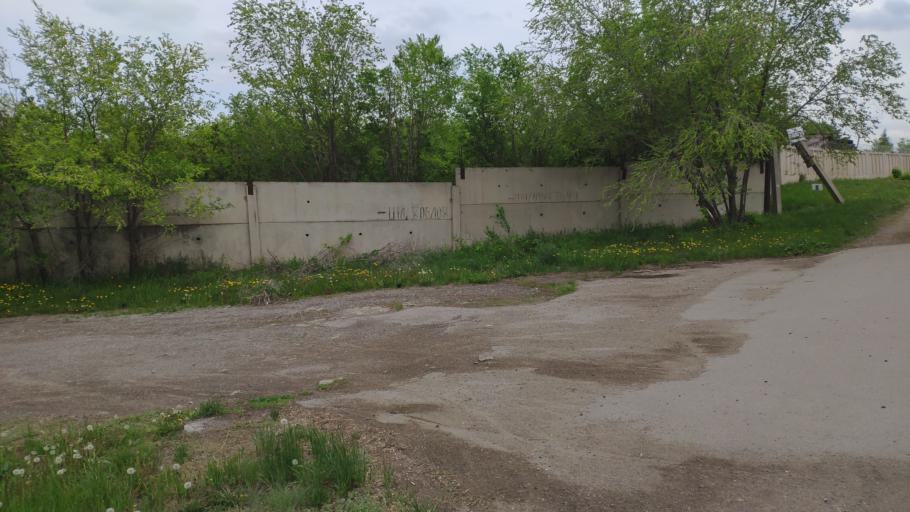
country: RU
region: Chelyabinsk
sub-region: Gorod Magnitogorsk
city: Magnitogorsk
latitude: 53.4151
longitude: 58.9563
